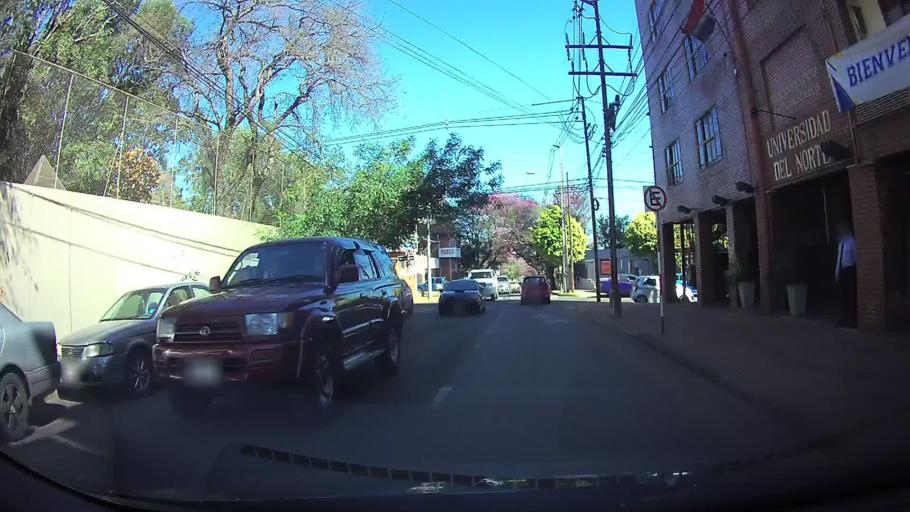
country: PY
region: Asuncion
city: Asuncion
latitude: -25.2846
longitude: -57.6169
